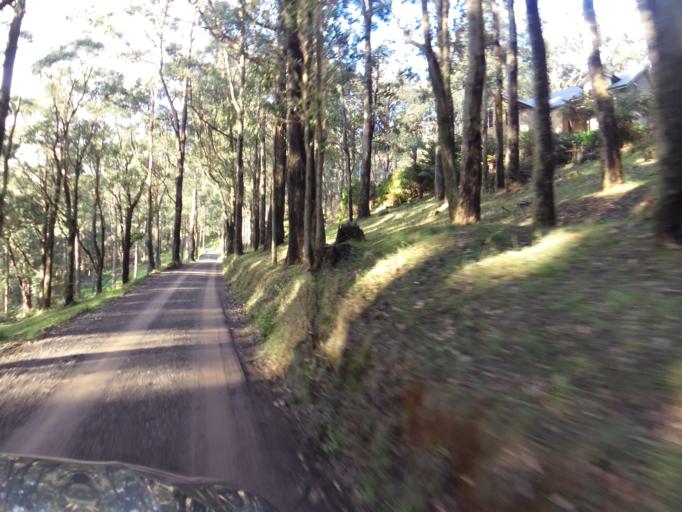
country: AU
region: Victoria
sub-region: Yarra Ranges
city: Ferny Creek
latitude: -37.8772
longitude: 145.3312
